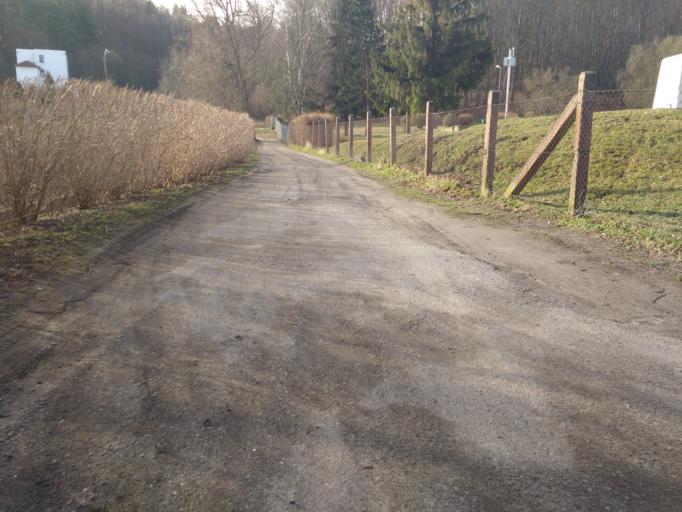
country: PL
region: Pomeranian Voivodeship
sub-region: Gdynia
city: Wielki Kack
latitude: 54.4836
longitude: 18.5155
